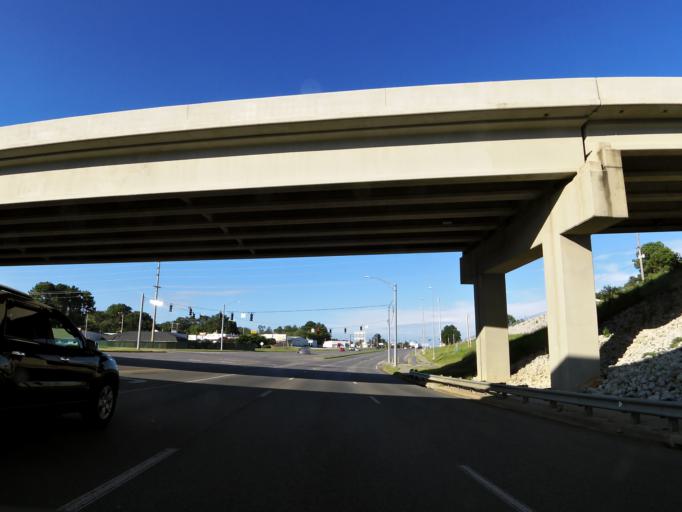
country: US
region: Alabama
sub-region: Lauderdale County
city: East Florence
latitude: 34.8149
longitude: -87.6639
